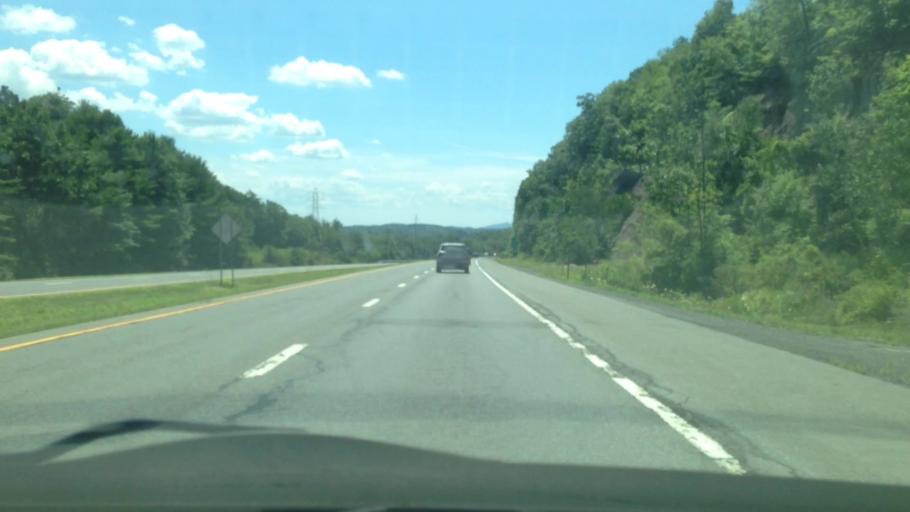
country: US
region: New York
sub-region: Ulster County
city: Lincoln Park
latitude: 41.9627
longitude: -74.0228
